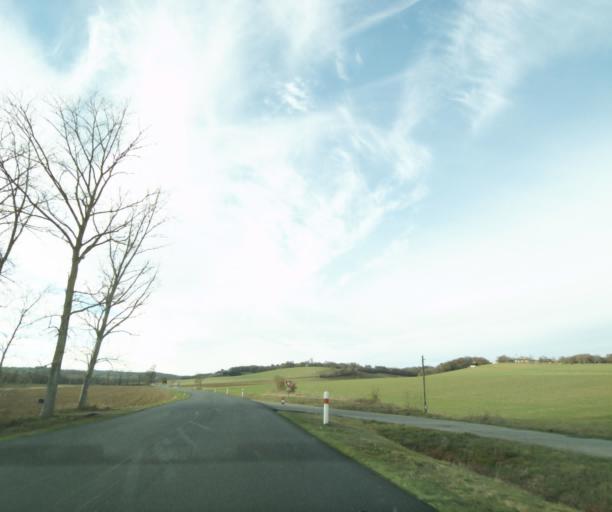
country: FR
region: Midi-Pyrenees
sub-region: Departement du Gers
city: Jegun
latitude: 43.6907
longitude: 0.4775
